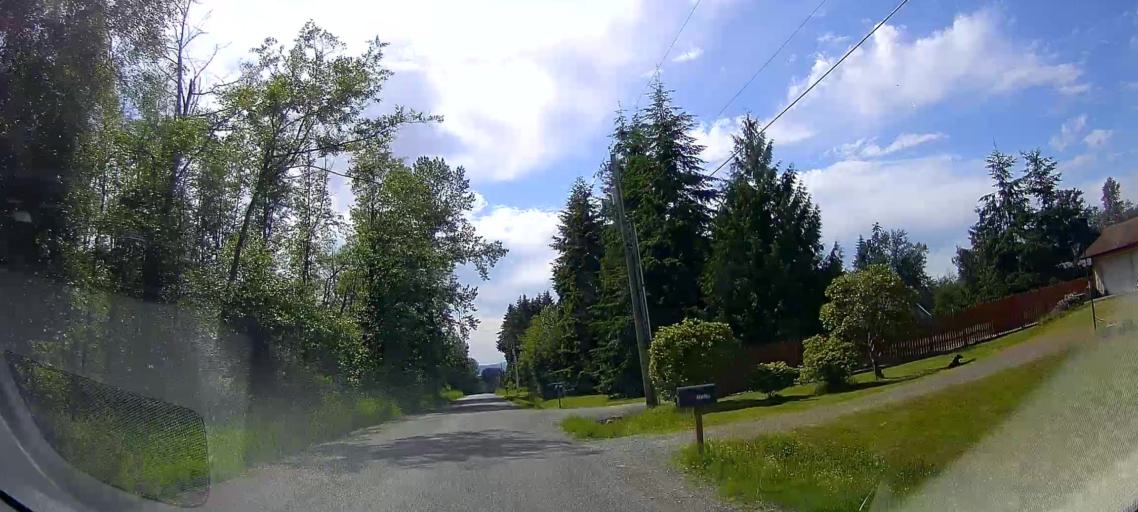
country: US
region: Washington
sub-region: Skagit County
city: Burlington
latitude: 48.5448
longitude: -122.3711
